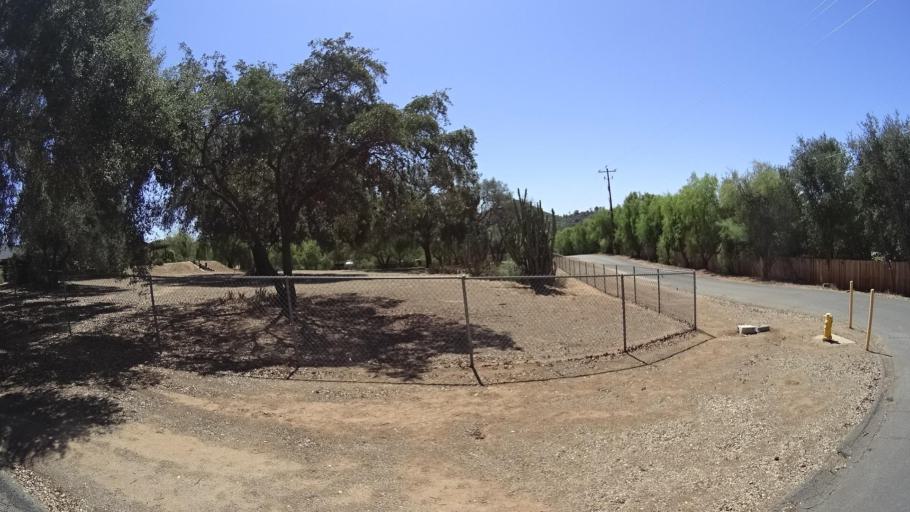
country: US
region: California
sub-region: San Diego County
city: Valley Center
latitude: 33.2727
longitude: -117.0102
